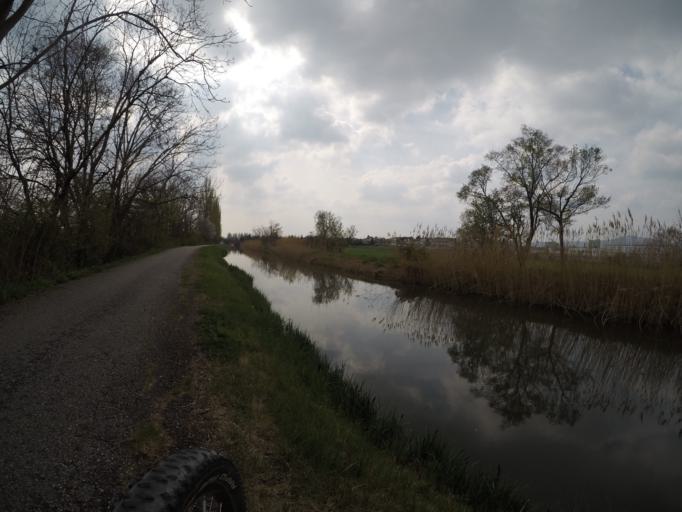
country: AT
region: Lower Austria
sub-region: Politischer Bezirk Baden
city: Pfaffstatten
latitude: 47.9973
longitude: 16.2590
